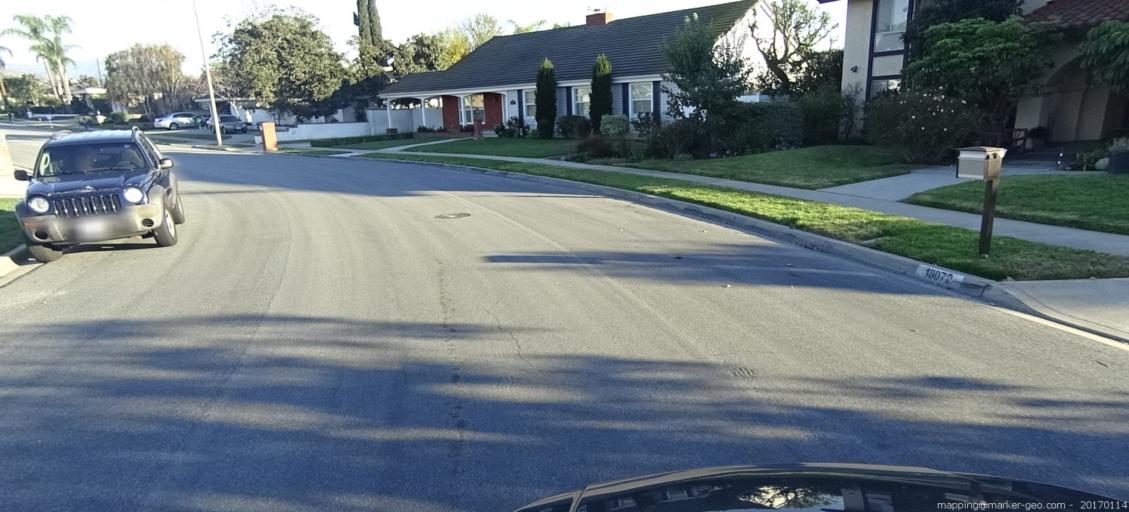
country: US
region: California
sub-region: Orange County
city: Tustin
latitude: 33.7632
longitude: -117.8178
